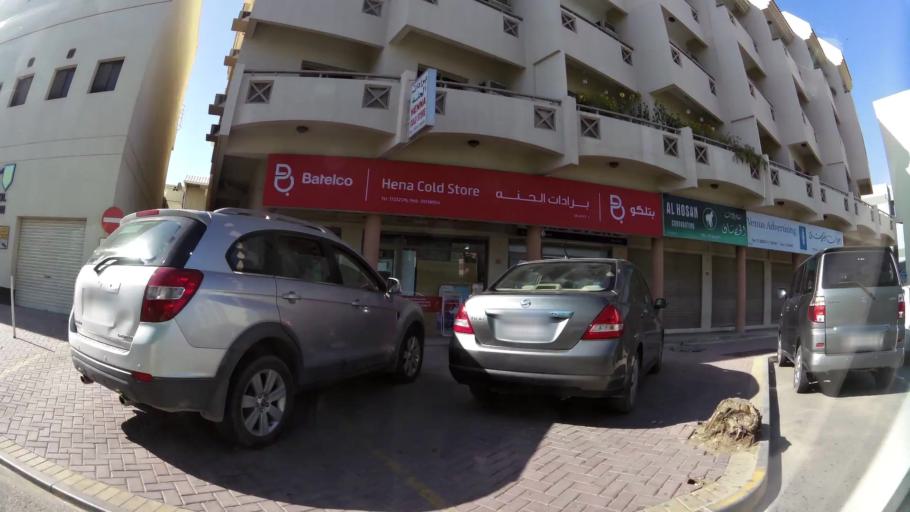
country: BH
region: Manama
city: Manama
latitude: 26.2275
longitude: 50.5803
